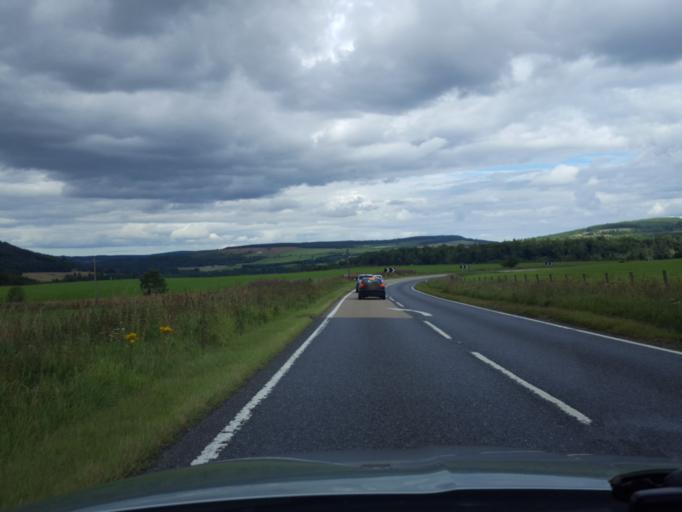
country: GB
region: Scotland
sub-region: Moray
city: Rothes
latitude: 57.4084
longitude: -3.3847
